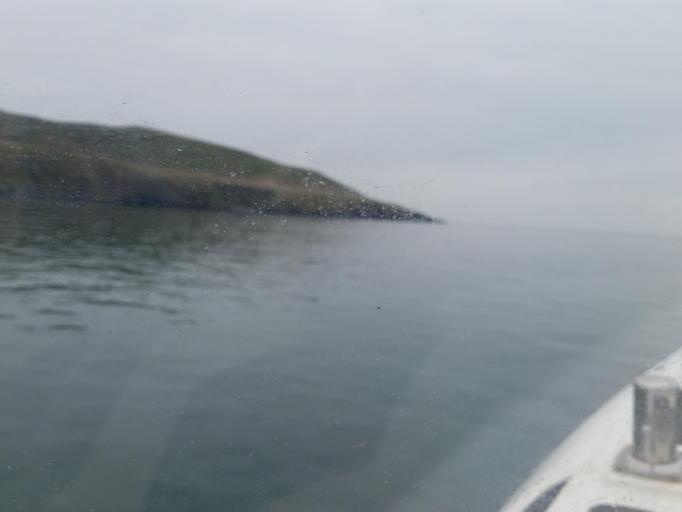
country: IE
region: Leinster
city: Portraine
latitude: 53.4812
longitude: -6.0250
